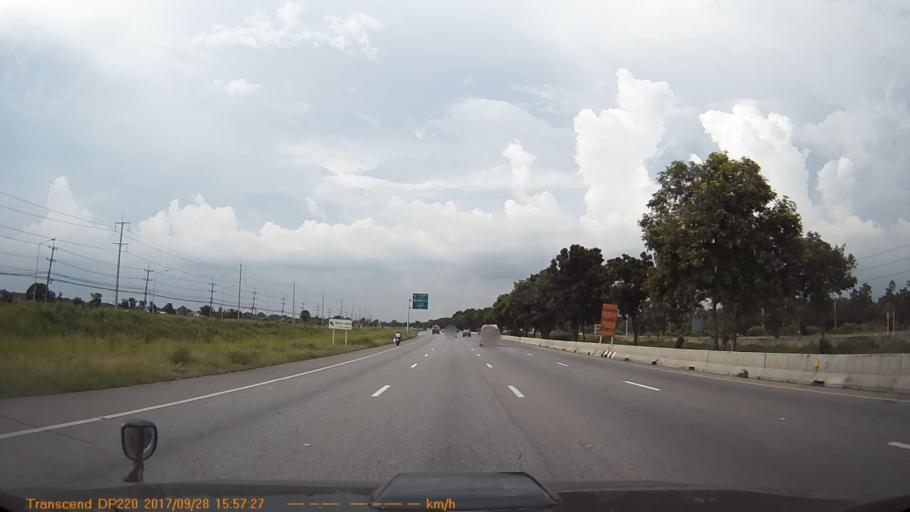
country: TH
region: Phra Nakhon Si Ayutthaya
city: Phra Nakhon Si Ayutthaya
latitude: 14.3601
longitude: 100.6127
